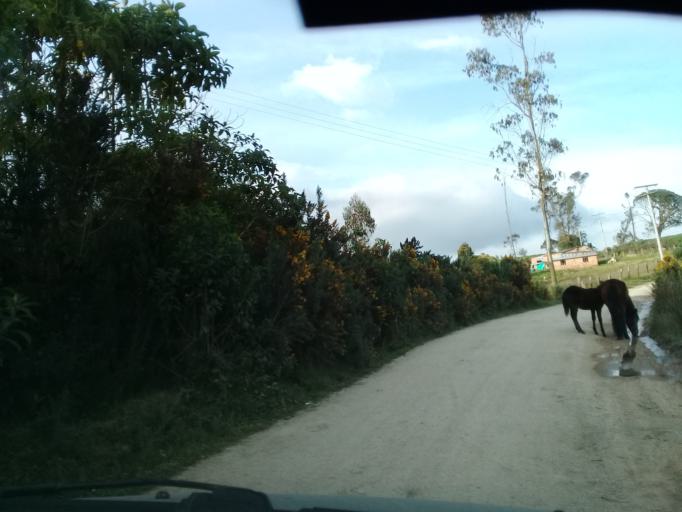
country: CO
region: Cundinamarca
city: Sibate
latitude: 4.4366
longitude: -74.2815
